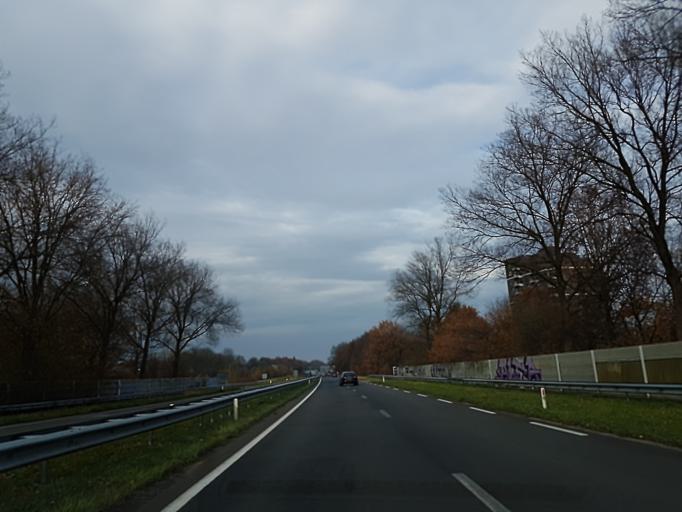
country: NL
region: North Brabant
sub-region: Roosendaal
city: Roosendaal
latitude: 51.5167
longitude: 4.4669
